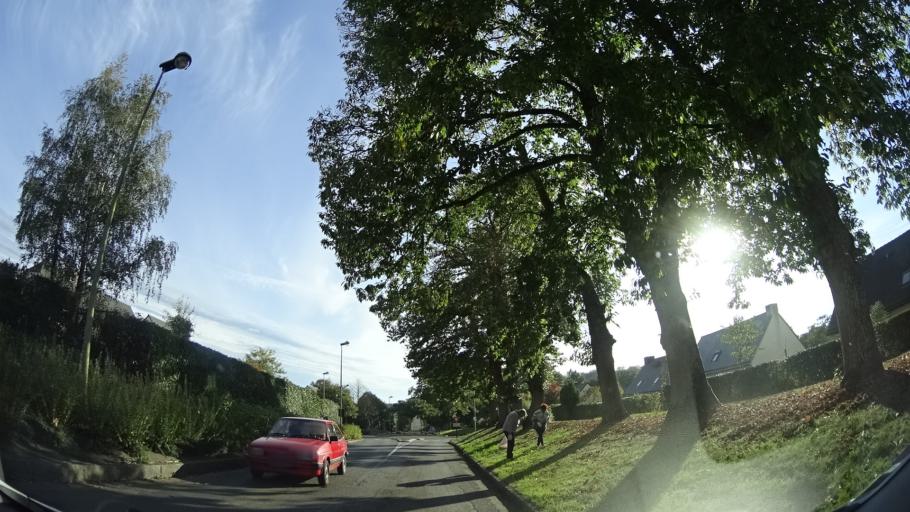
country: FR
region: Brittany
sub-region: Departement d'Ille-et-Vilaine
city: Geveze
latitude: 48.2163
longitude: -1.7912
